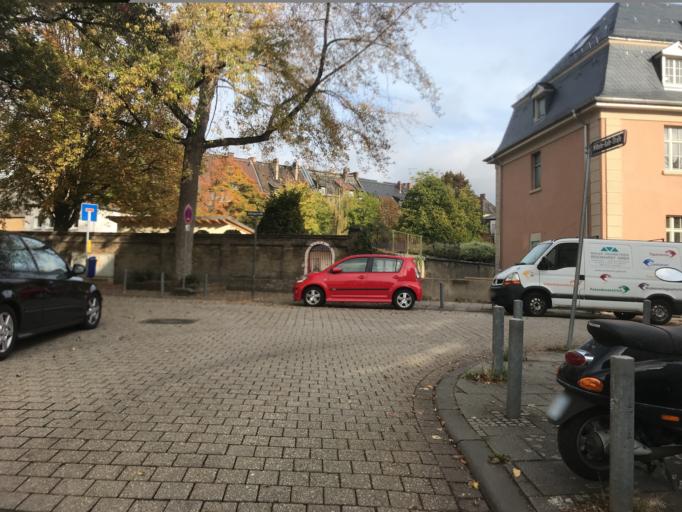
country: DE
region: Hesse
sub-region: Regierungsbezirk Darmstadt
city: Wiesbaden
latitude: 50.0390
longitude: 8.2421
